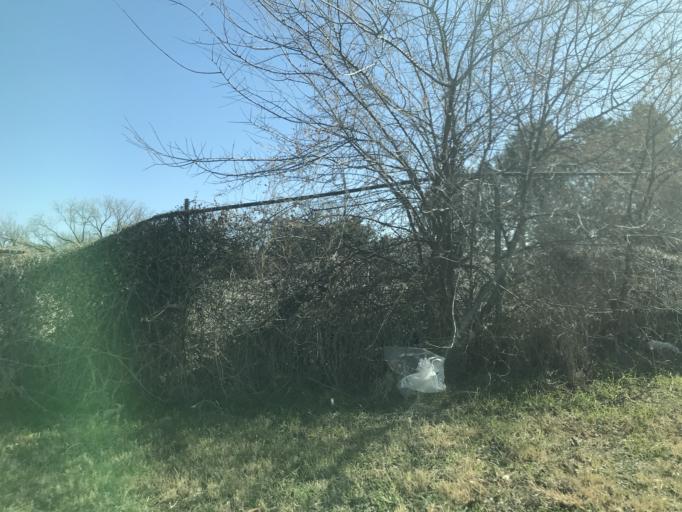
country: US
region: Texas
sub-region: Taylor County
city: Abilene
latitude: 32.4643
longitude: -99.7215
